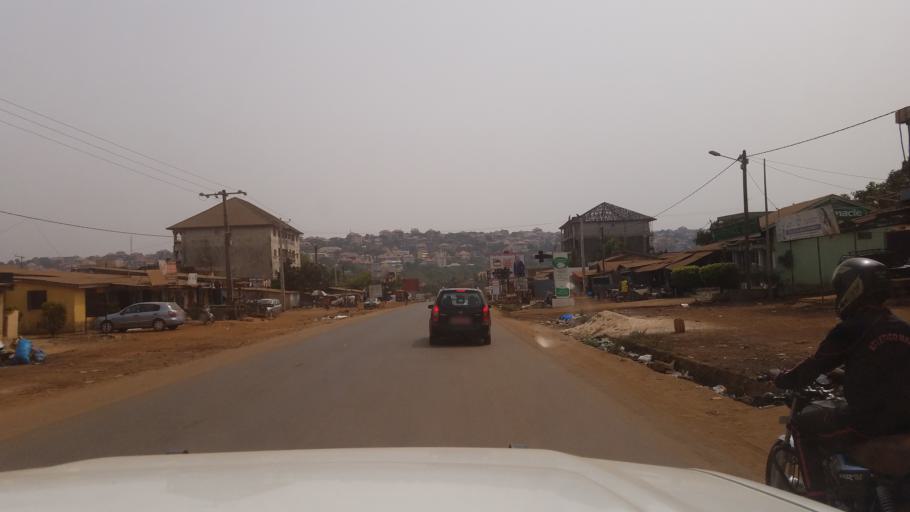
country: GN
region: Conakry
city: Conakry
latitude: 9.6460
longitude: -13.6074
